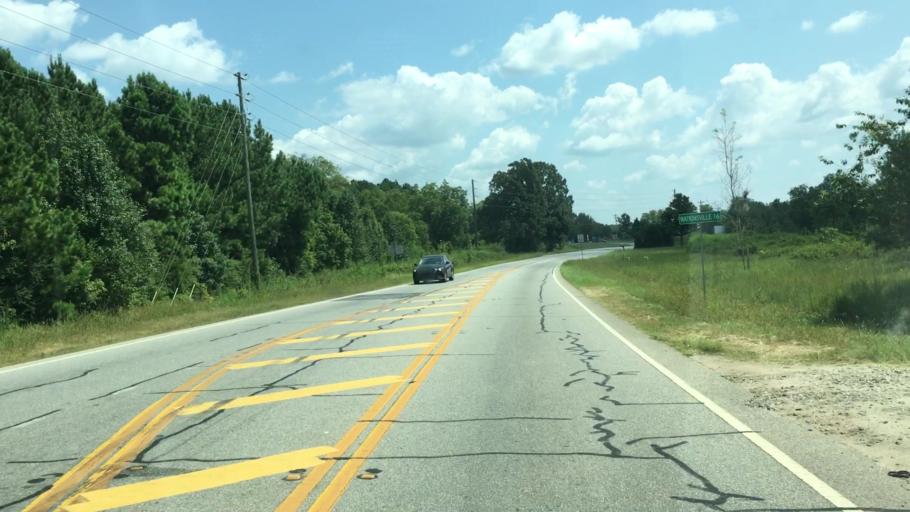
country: US
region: Georgia
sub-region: Barrow County
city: Russell
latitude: 33.9555
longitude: -83.6553
